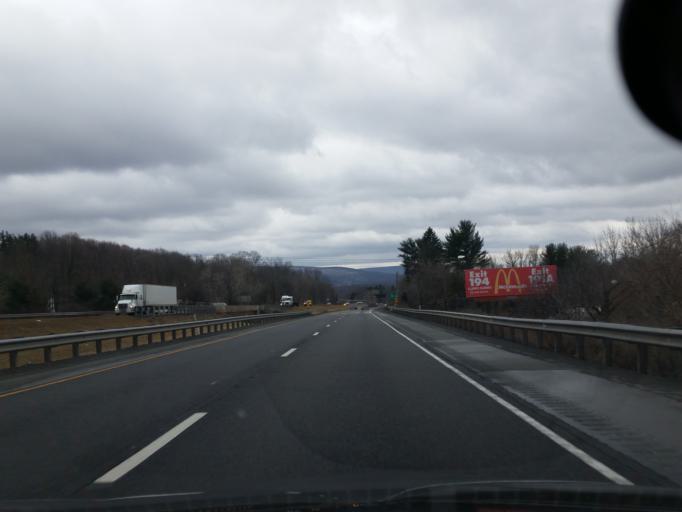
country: US
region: Pennsylvania
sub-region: Lackawanna County
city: Clarks Green
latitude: 41.5135
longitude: -75.6667
